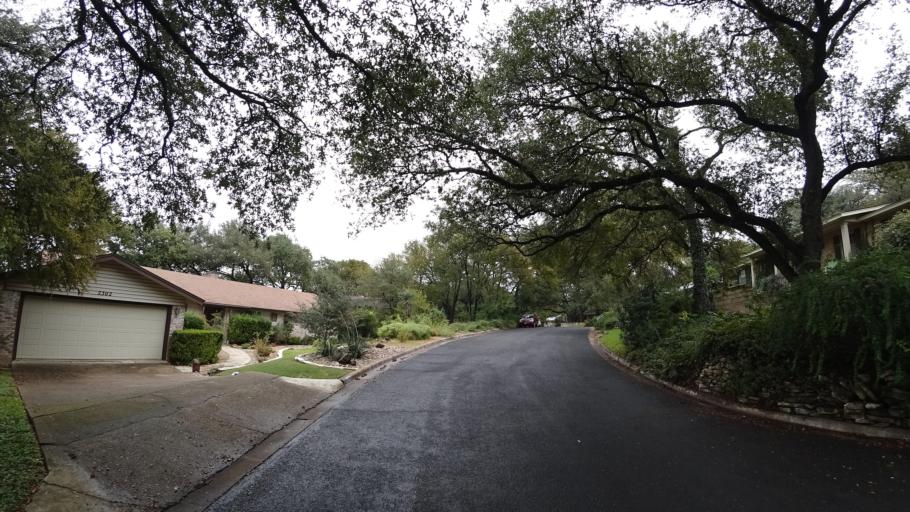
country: US
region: Texas
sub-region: Travis County
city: Rollingwood
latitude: 30.2587
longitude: -97.7747
